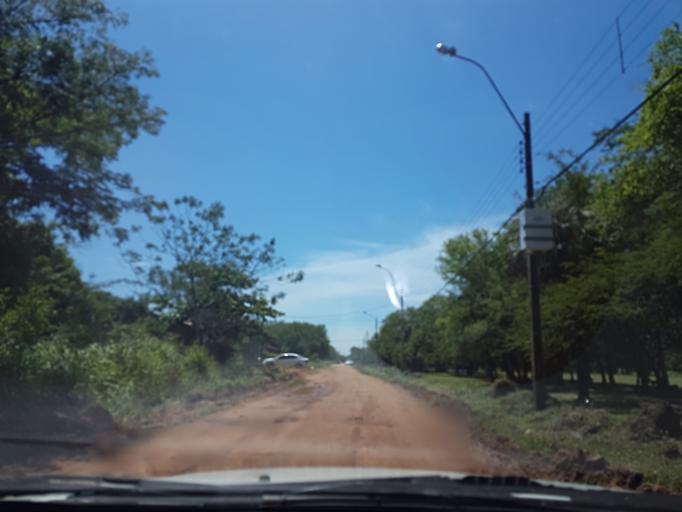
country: PY
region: Central
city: Limpio
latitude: -25.1881
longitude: -57.4850
